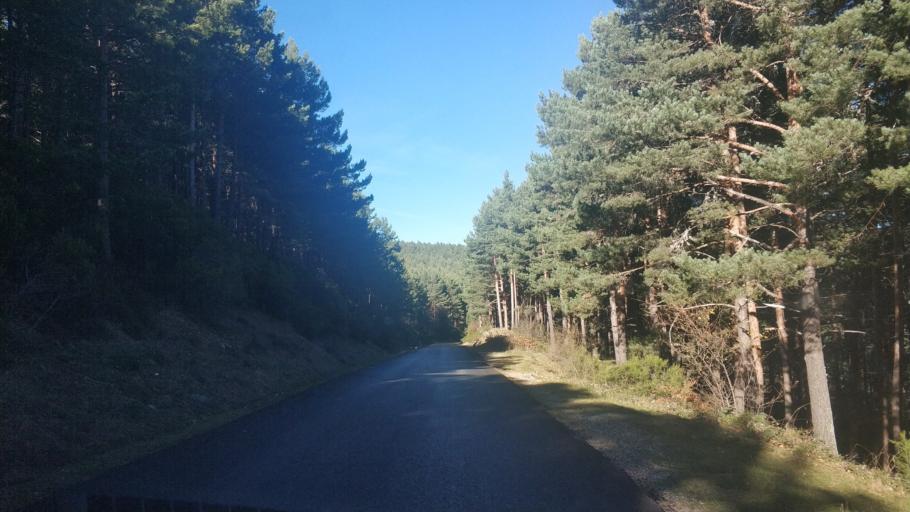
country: ES
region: Castille and Leon
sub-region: Provincia de Soria
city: Covaleda
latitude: 41.9977
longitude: -2.8130
